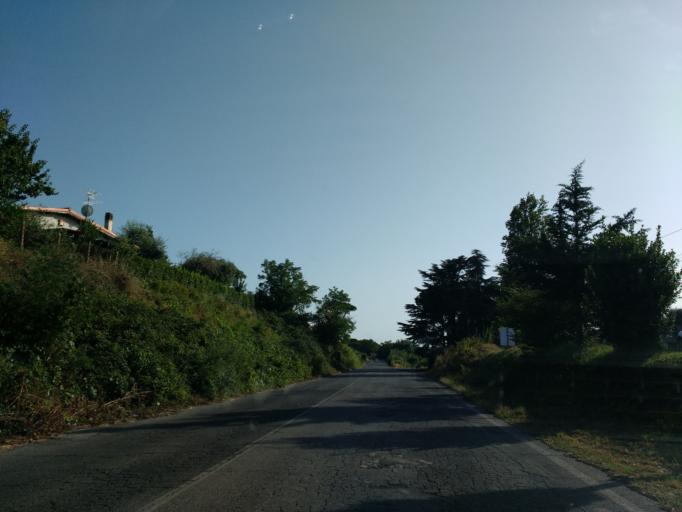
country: IT
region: Latium
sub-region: Citta metropolitana di Roma Capitale
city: Marino
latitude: 41.7560
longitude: 12.6391
